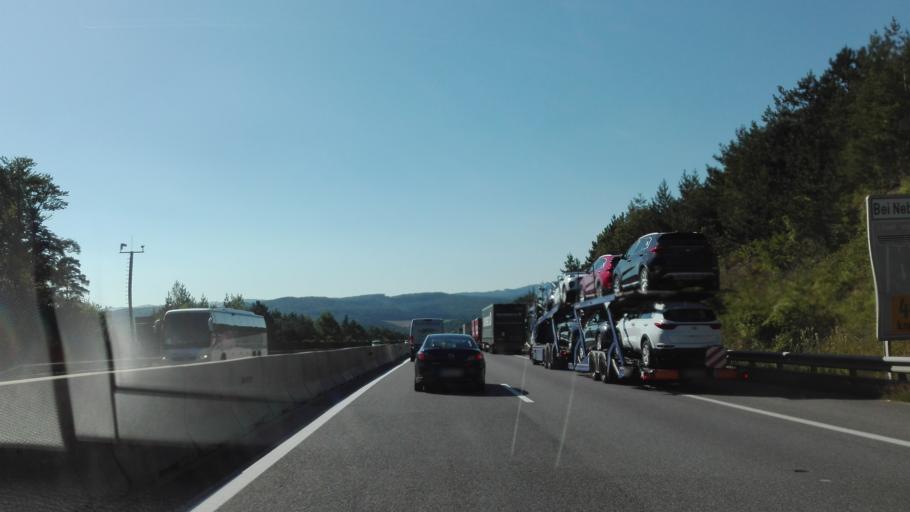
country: AT
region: Lower Austria
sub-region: Politischer Bezirk Baden
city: Heiligenkreuz
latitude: 48.0577
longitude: 16.1462
